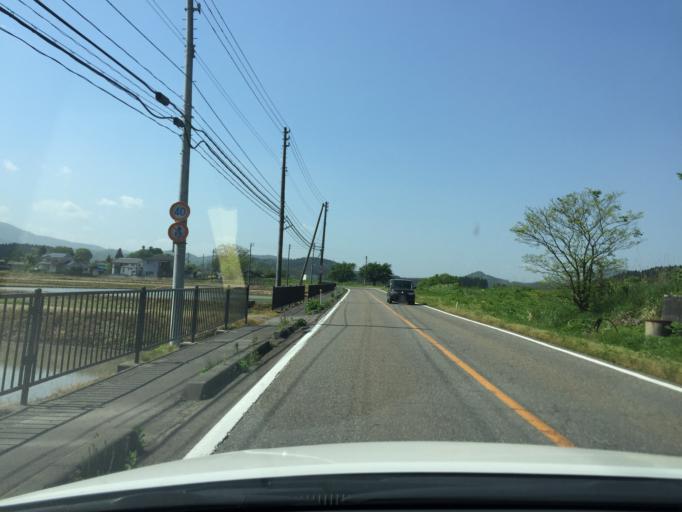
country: JP
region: Niigata
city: Muramatsu
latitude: 37.6813
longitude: 139.1501
